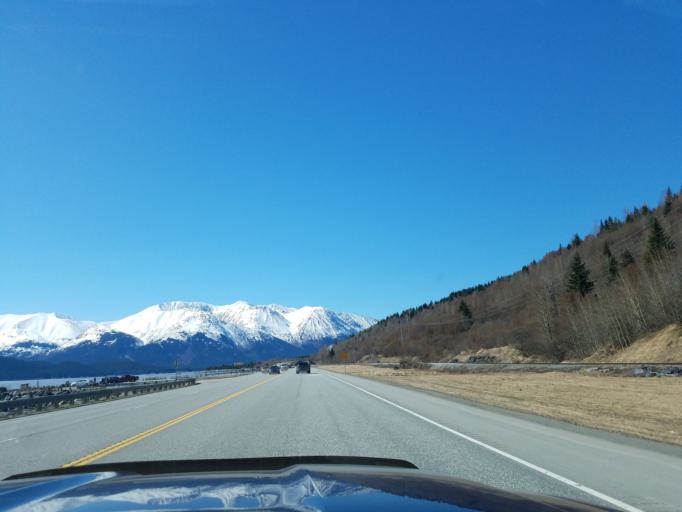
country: US
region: Alaska
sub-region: Anchorage Municipality
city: Girdwood
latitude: 60.9333
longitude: -149.3209
